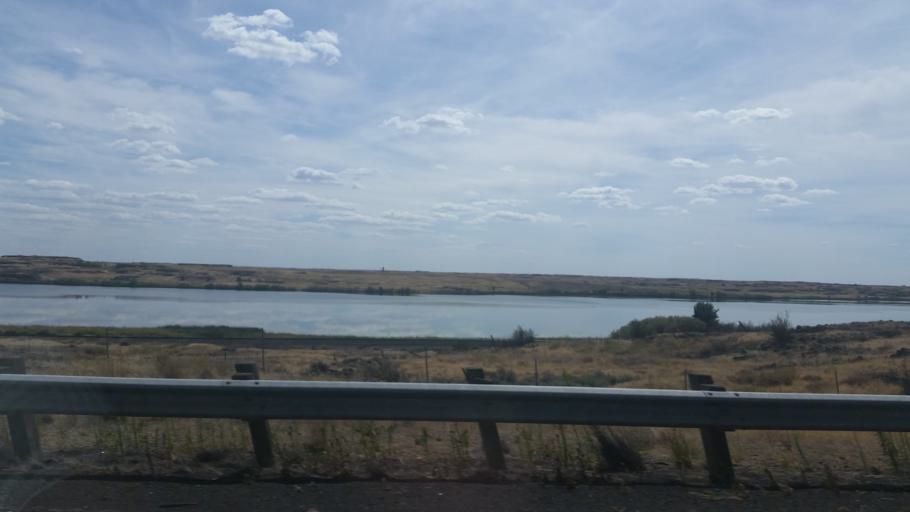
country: US
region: Washington
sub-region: Adams County
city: Ritzville
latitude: 47.2763
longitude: -118.0544
